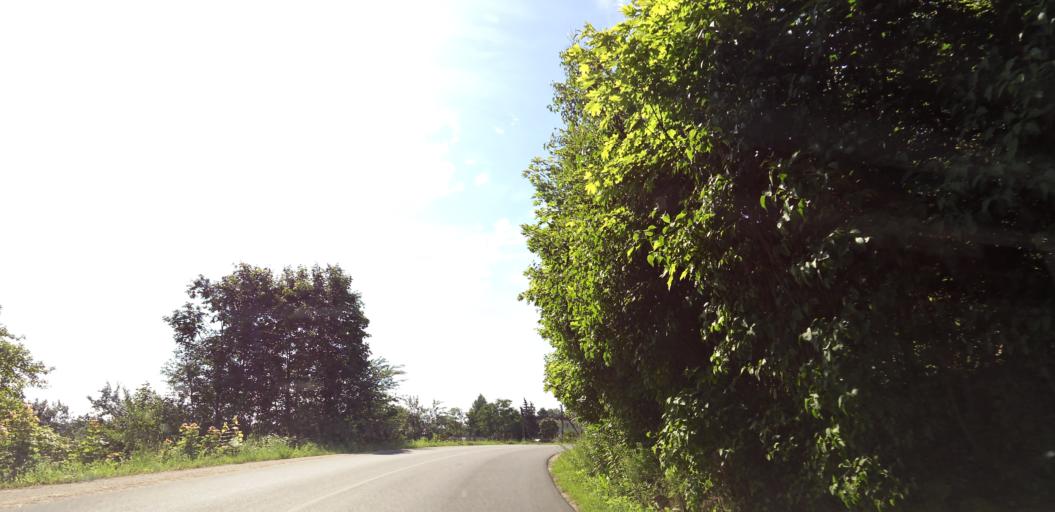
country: LT
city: Grigiskes
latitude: 54.7810
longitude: 25.0878
